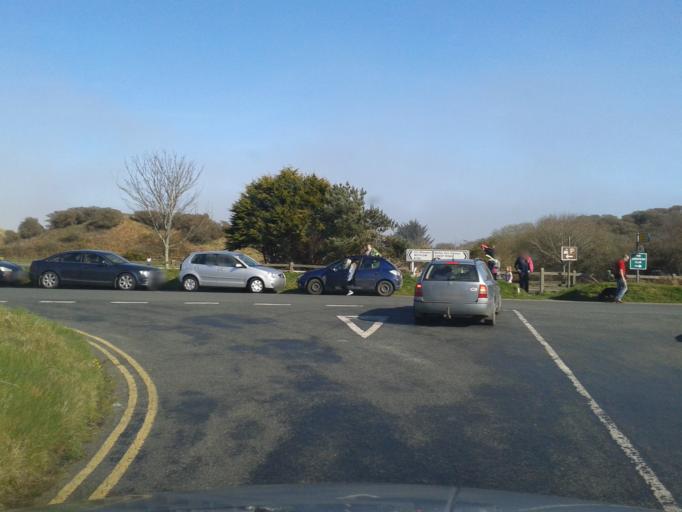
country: IE
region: Leinster
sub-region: Wicklow
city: Wicklow
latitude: 52.8771
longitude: -6.0651
